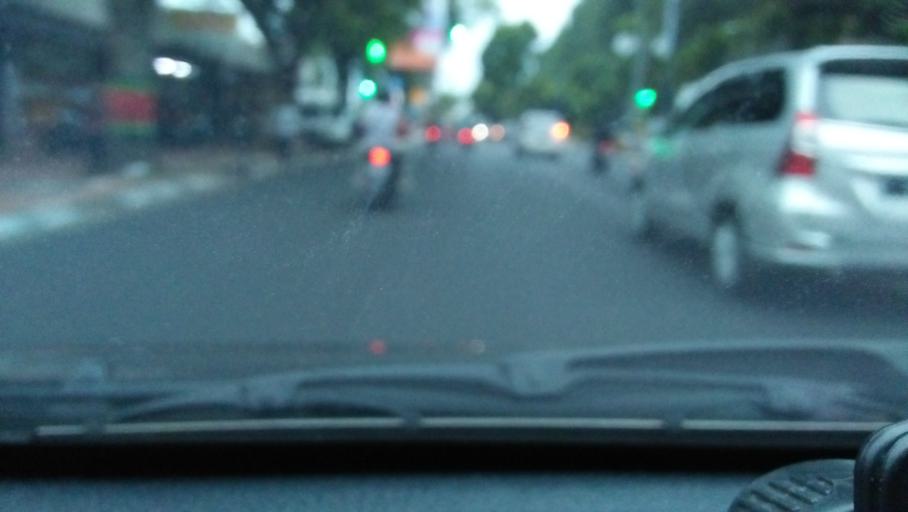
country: ID
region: Central Java
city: Magelang
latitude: -7.4931
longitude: 110.2228
